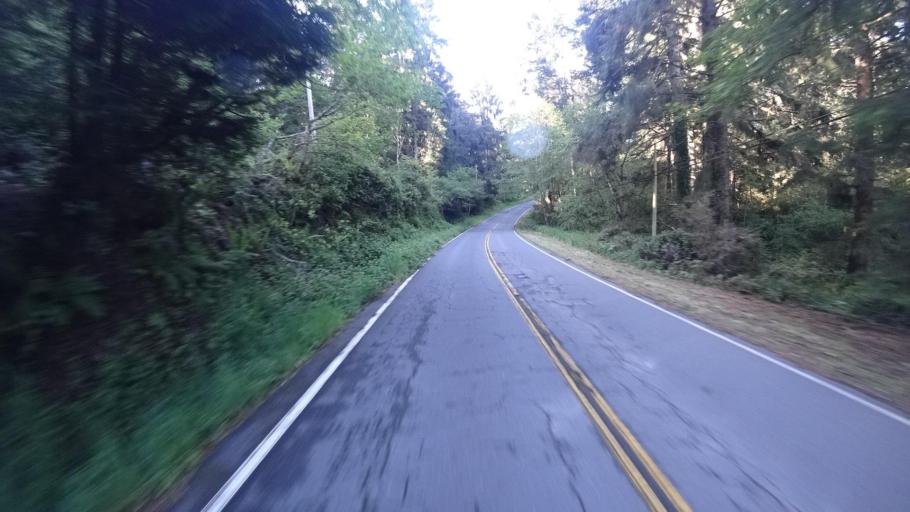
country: US
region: California
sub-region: Humboldt County
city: Westhaven-Moonstone
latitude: 41.1149
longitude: -124.1561
